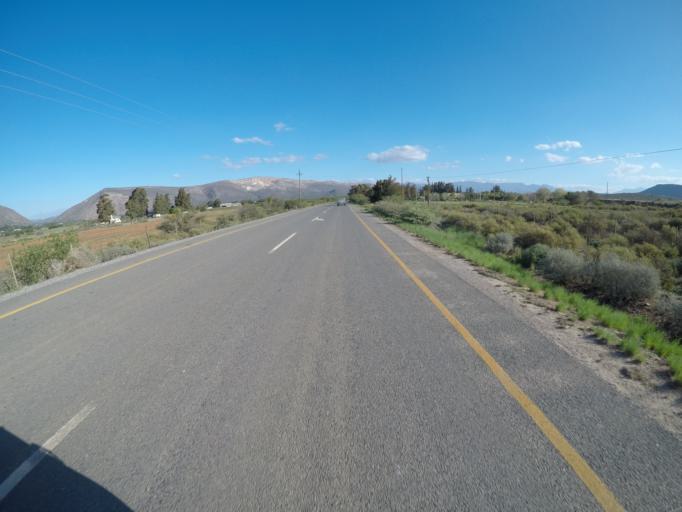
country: ZA
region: Western Cape
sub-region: Cape Winelands District Municipality
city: Ashton
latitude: -33.8073
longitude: 19.7823
